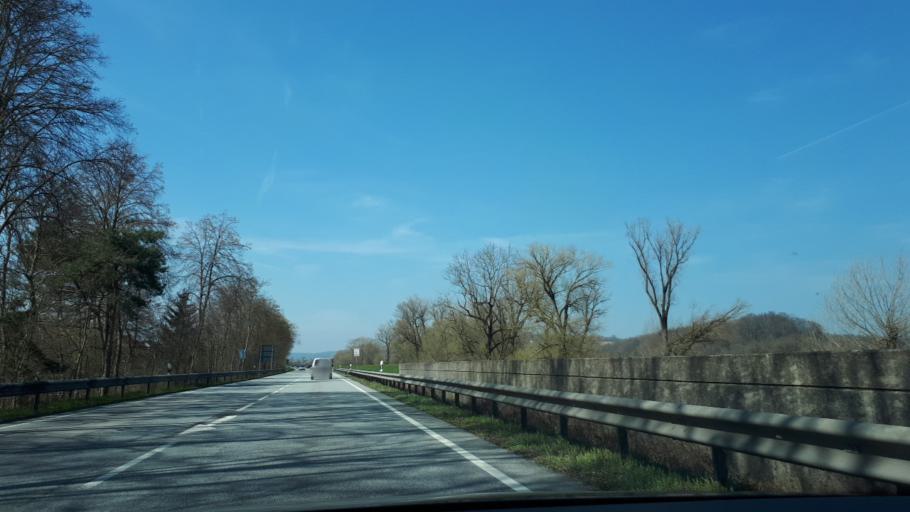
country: DE
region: Bavaria
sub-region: Lower Bavaria
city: Saal
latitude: 48.9051
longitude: 11.9461
